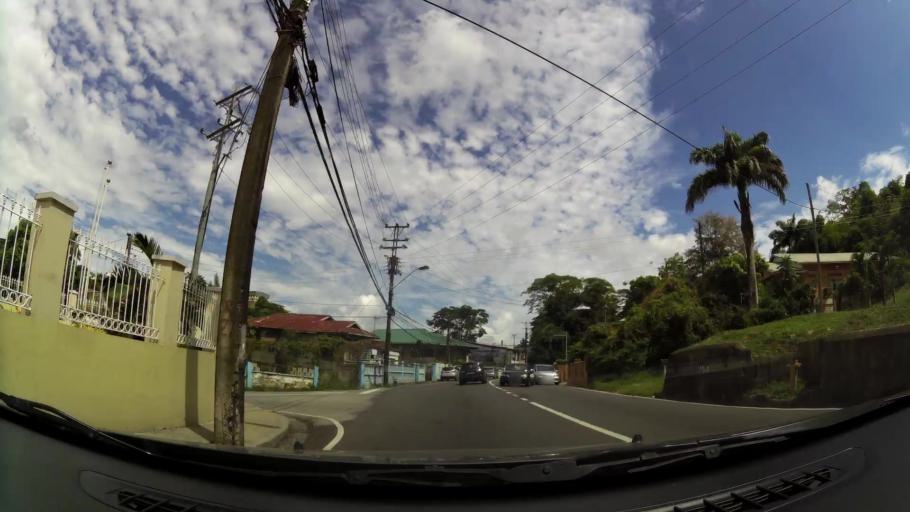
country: TT
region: City of San Fernando
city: San Fernando
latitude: 10.2832
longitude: -61.4612
